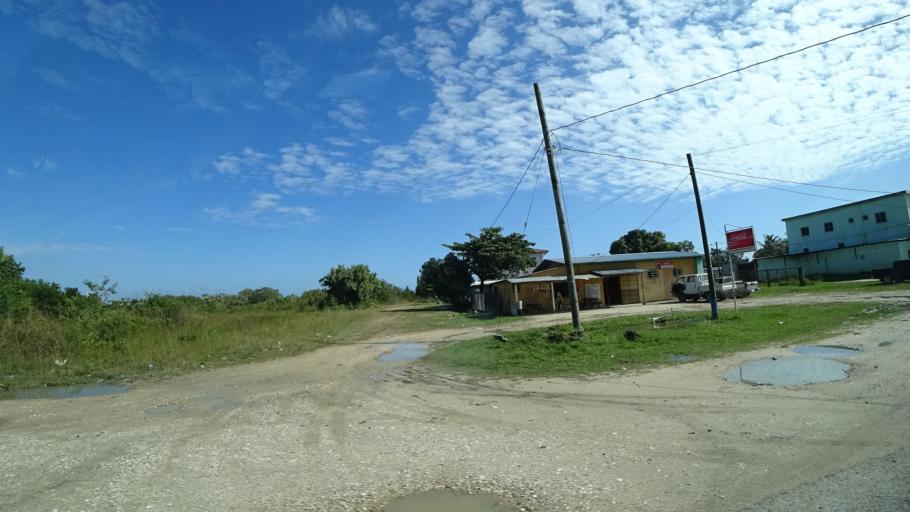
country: BZ
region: Belize
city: Belize City
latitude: 17.5760
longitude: -88.3394
